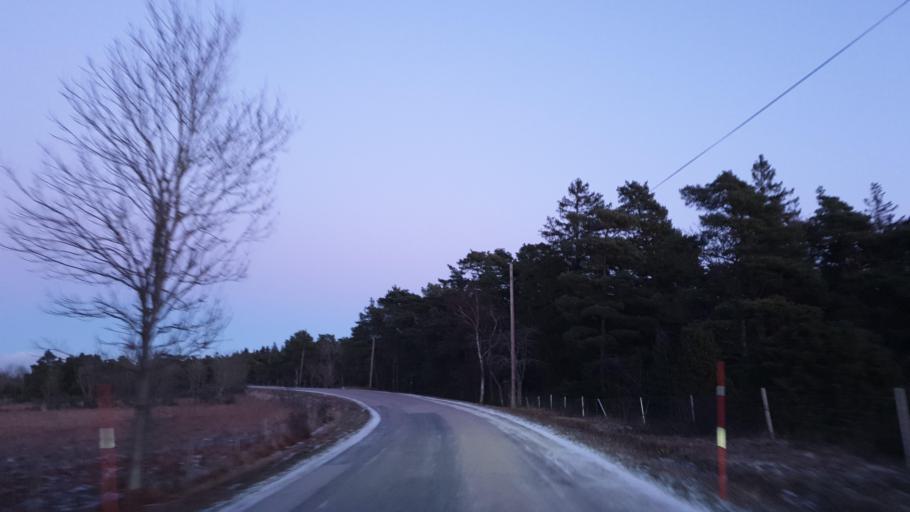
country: SE
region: Gotland
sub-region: Gotland
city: Slite
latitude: 57.4178
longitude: 18.8161
